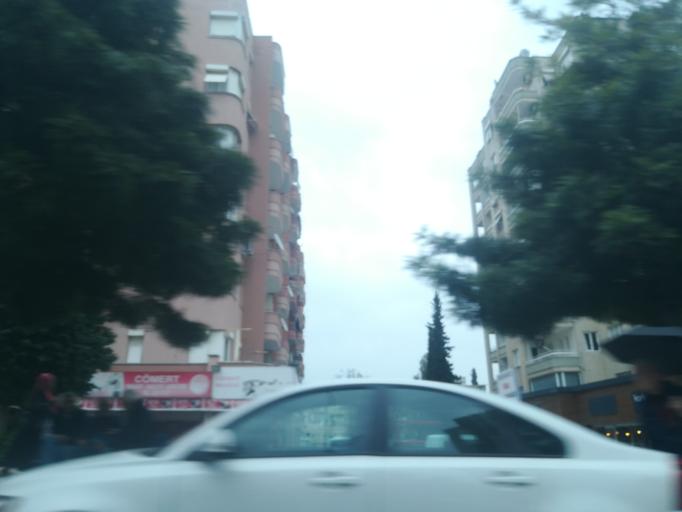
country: TR
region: Adana
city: Adana
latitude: 37.0339
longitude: 35.3083
